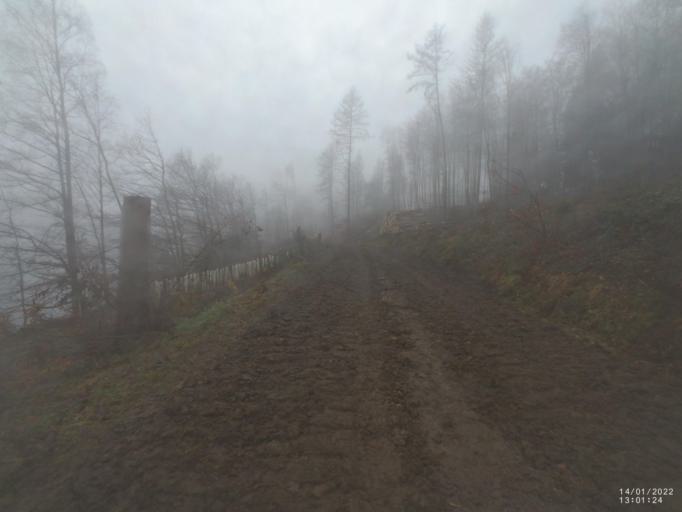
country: DE
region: North Rhine-Westphalia
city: Meinerzhagen
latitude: 51.0796
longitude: 7.6262
